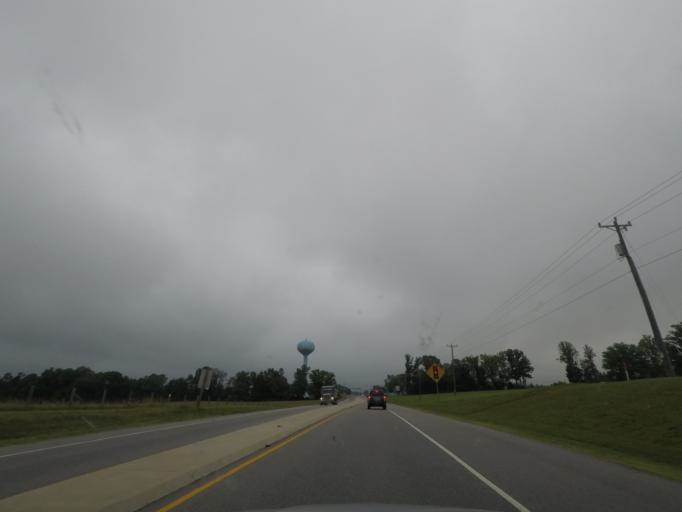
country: US
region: Virginia
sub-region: Prince Edward County
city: Farmville
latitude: 37.2609
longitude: -78.4118
